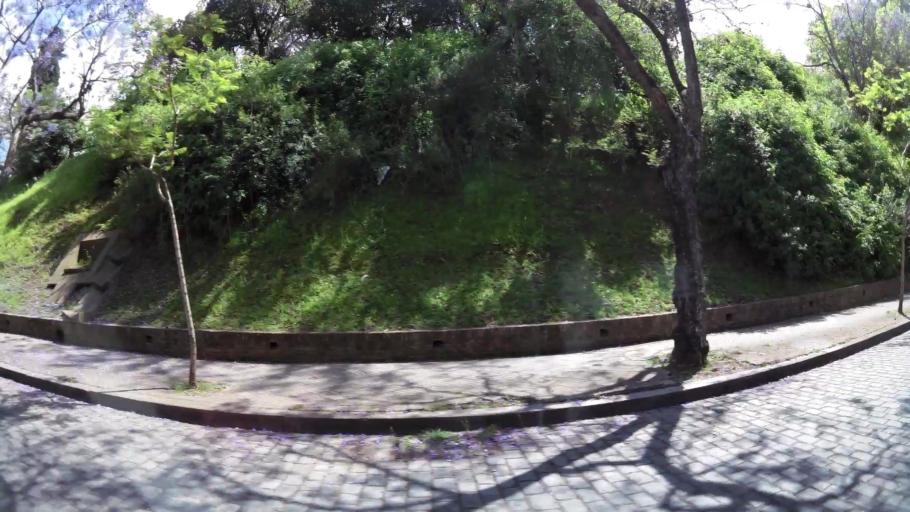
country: AR
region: Santa Fe
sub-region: Departamento de Rosario
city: Rosario
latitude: -32.9602
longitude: -60.6240
